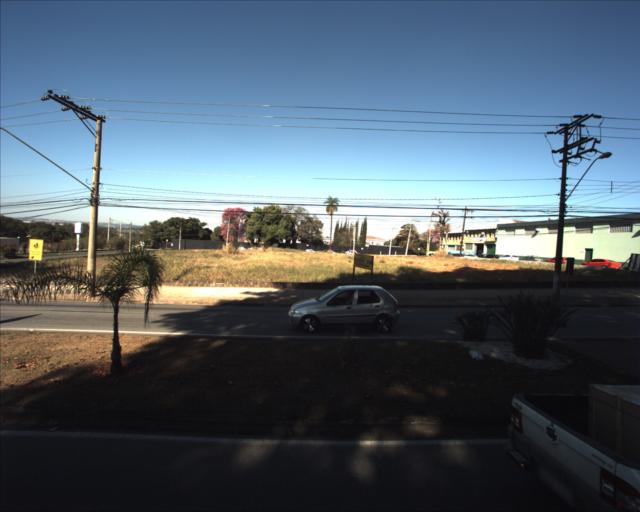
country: BR
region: Sao Paulo
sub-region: Sorocaba
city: Sorocaba
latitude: -23.4181
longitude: -47.4088
